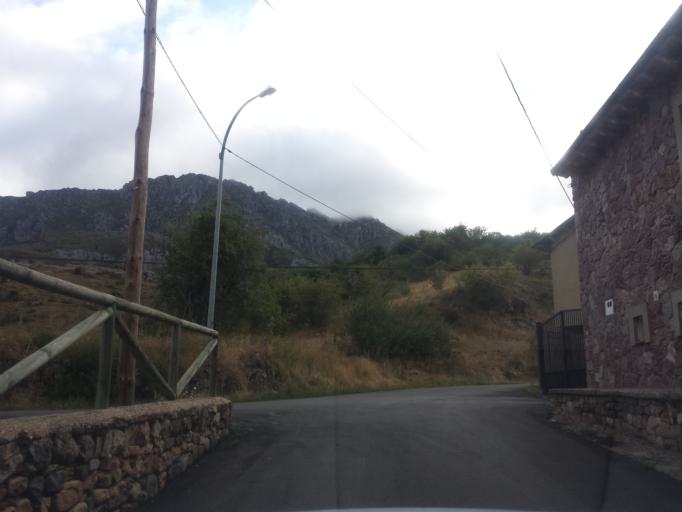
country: ES
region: Castille and Leon
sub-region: Provincia de Leon
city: Carmenes
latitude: 42.9527
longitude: -5.5628
